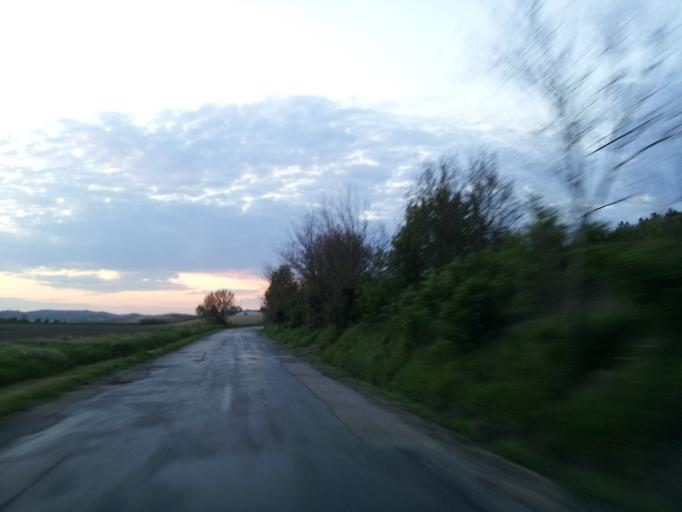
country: HU
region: Komarom-Esztergom
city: Csolnok
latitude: 47.6502
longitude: 18.7157
